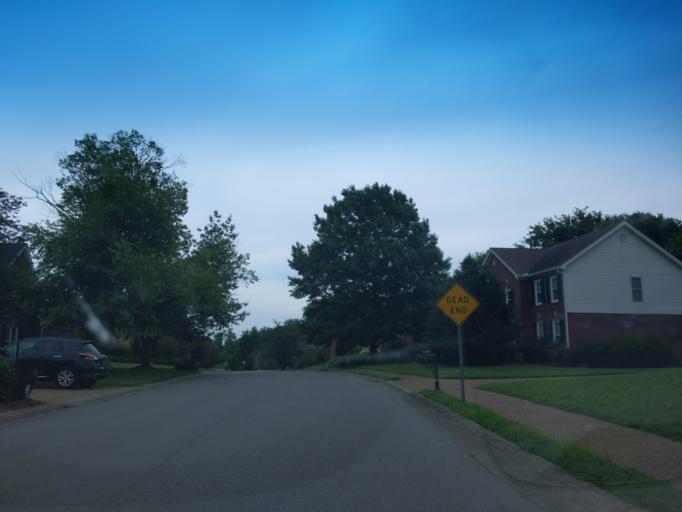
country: US
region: Tennessee
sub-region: Williamson County
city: Brentwood Estates
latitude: 36.0368
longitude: -86.7615
